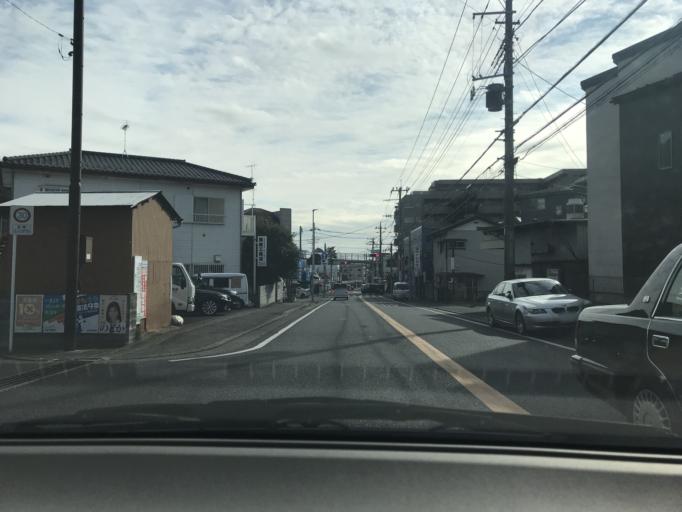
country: JP
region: Tokyo
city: Chofugaoka
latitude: 35.6035
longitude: 139.5782
